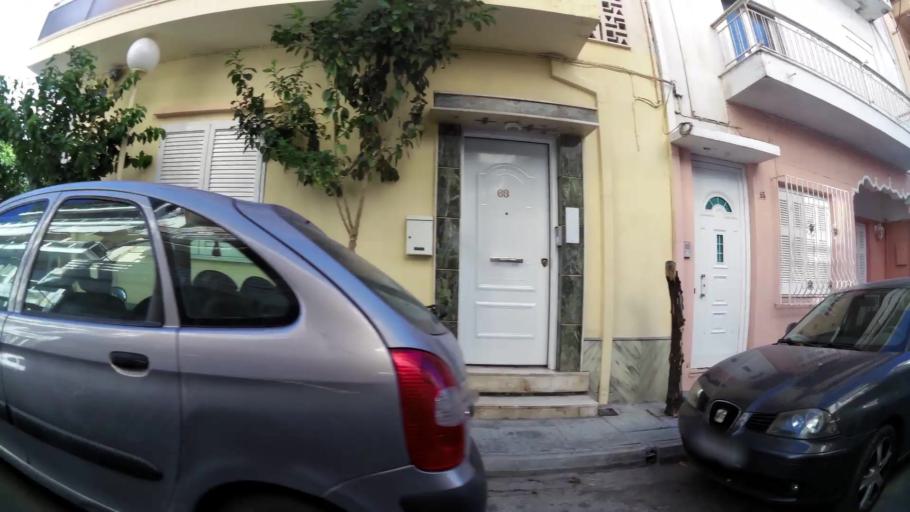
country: GR
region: Attica
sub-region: Nomos Piraios
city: Nikaia
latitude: 37.9664
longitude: 23.6557
